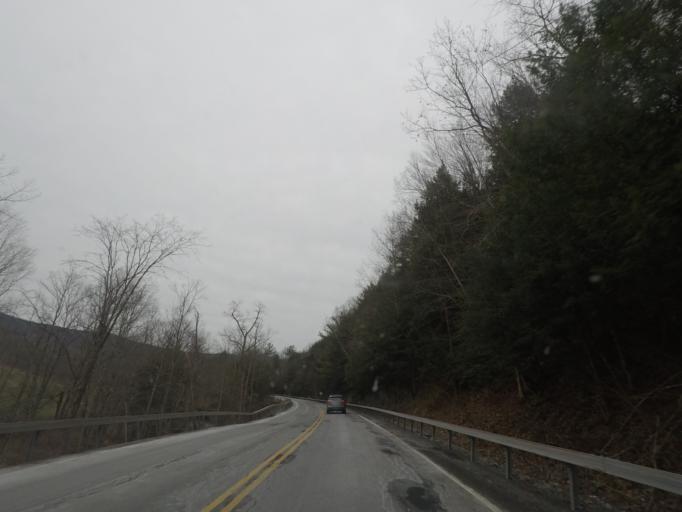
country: US
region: Massachusetts
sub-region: Berkshire County
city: Williamstown
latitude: 42.7441
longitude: -73.3195
